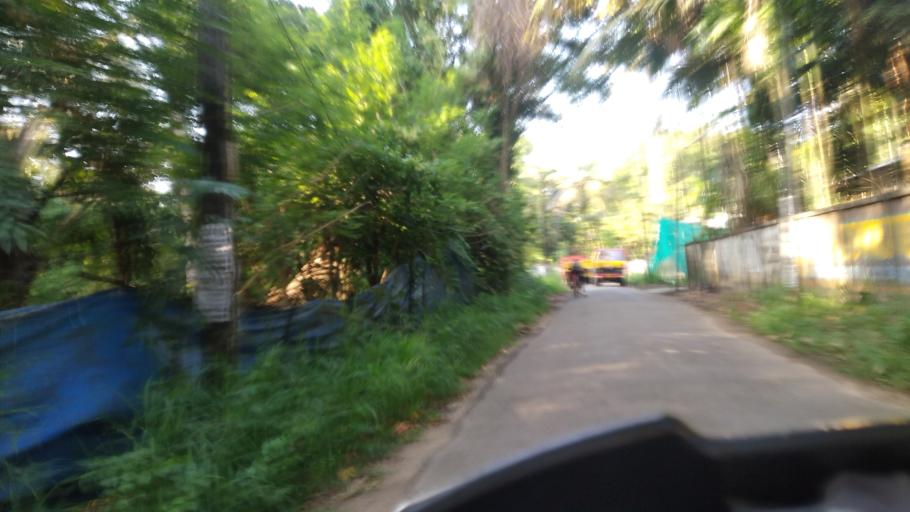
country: IN
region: Kerala
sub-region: Ernakulam
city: Elur
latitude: 10.0413
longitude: 76.2278
